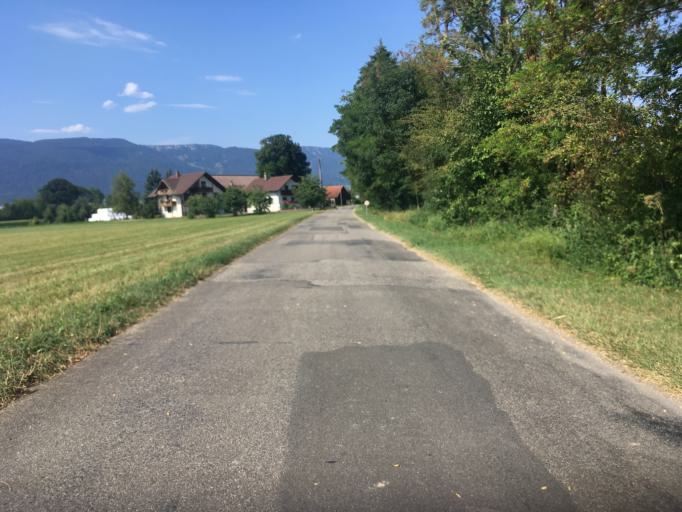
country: CH
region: Bern
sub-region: Biel/Bienne District
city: Lengnau
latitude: 47.1564
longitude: 7.3877
